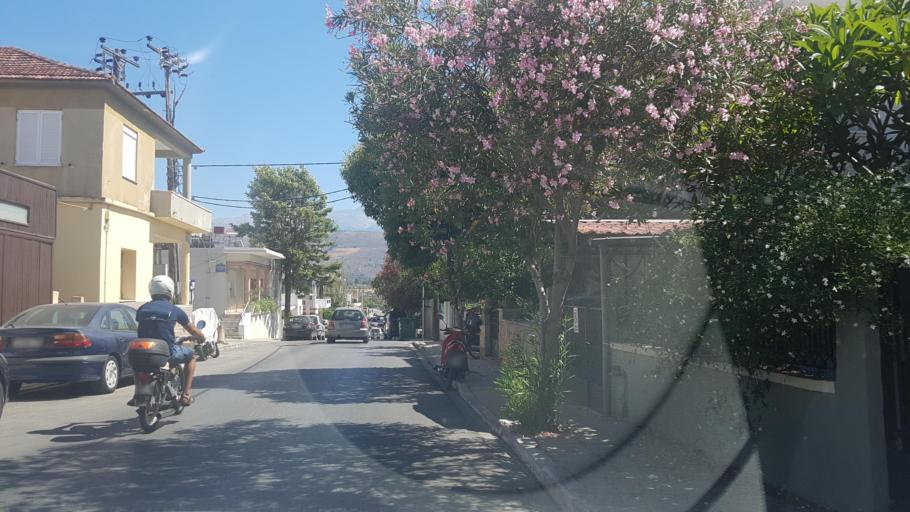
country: GR
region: Crete
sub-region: Nomos Chanias
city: Chania
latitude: 35.5057
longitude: 24.0177
